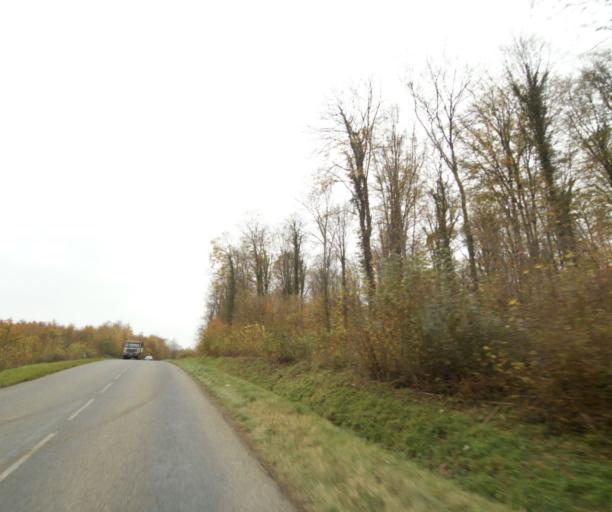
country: FR
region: Lorraine
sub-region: Departement de Meurthe-et-Moselle
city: Joeuf
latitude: 49.2557
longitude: 5.9997
